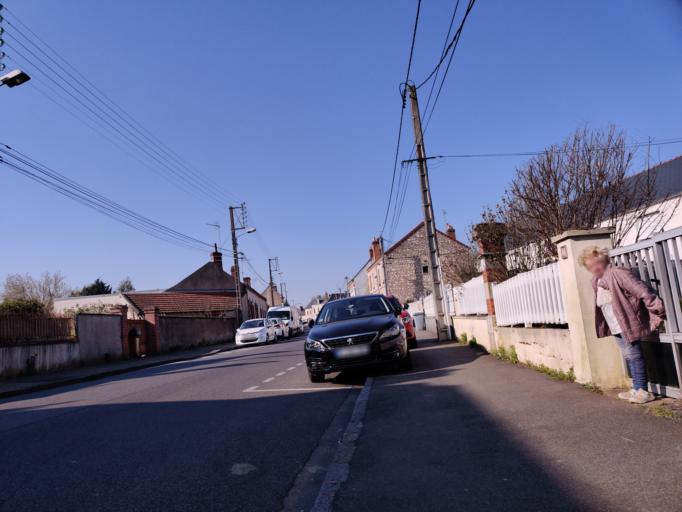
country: FR
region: Centre
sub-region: Departement du Loiret
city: Fleury-les-Aubrais
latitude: 47.9245
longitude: 1.9253
